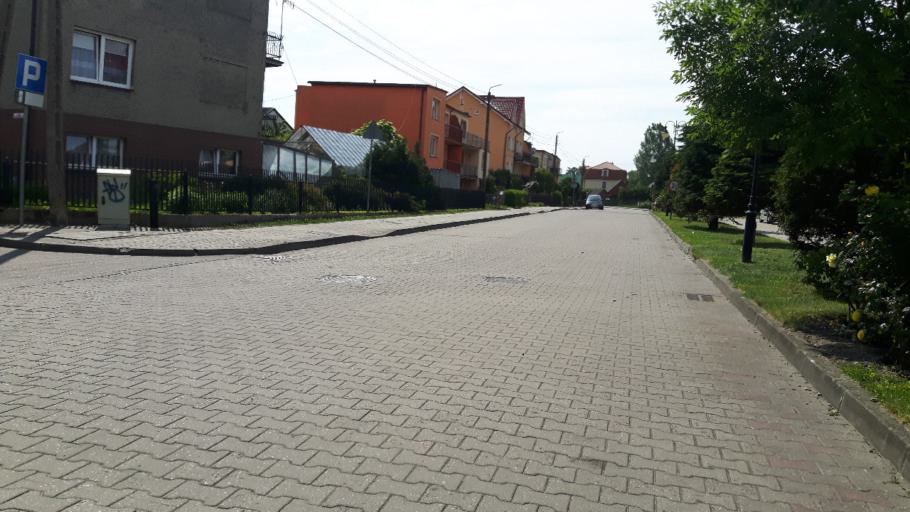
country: PL
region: Pomeranian Voivodeship
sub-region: Powiat leborski
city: Leba
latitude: 54.7571
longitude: 17.5597
